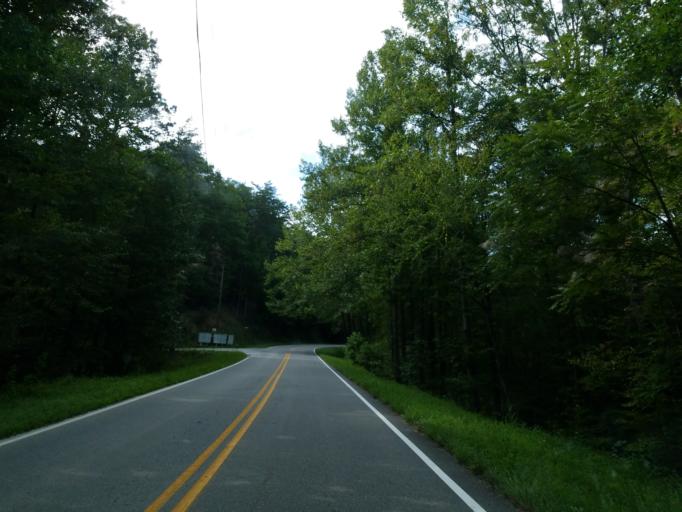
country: US
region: Georgia
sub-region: Gilmer County
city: Ellijay
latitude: 34.7530
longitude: -84.4224
